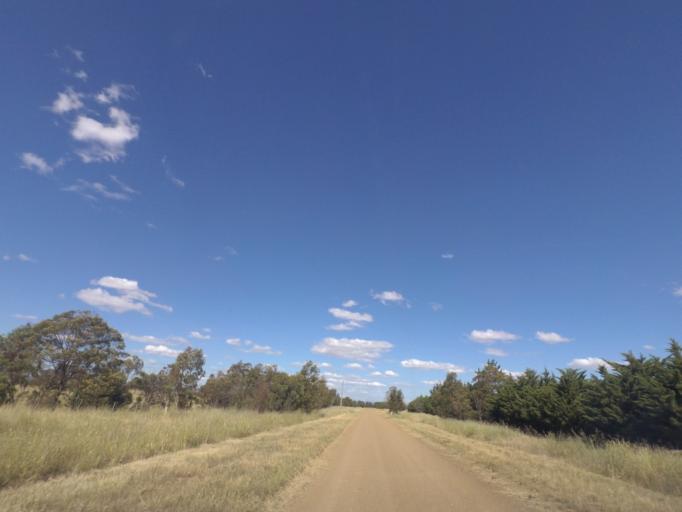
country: AU
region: Victoria
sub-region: Hume
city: Sunbury
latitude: -37.4617
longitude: 144.8157
